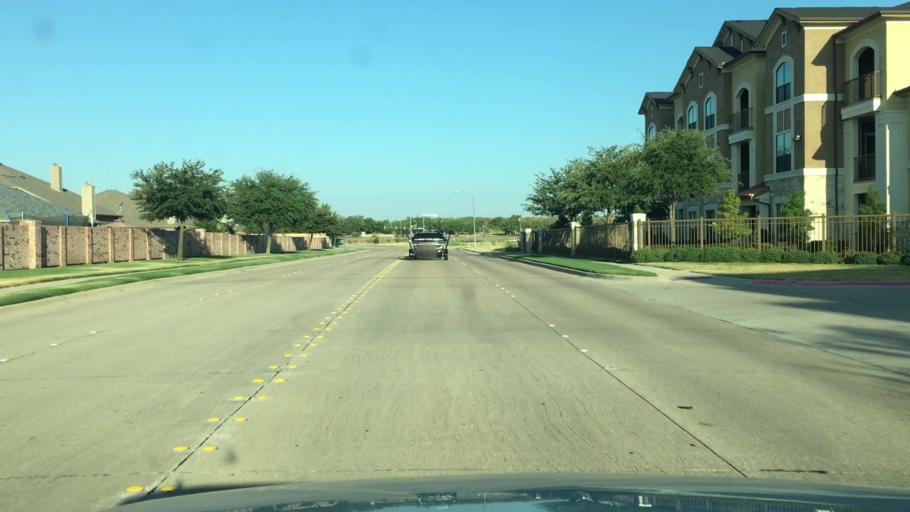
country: US
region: Texas
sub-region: Tarrant County
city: Crowley
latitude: 32.5510
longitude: -97.3615
